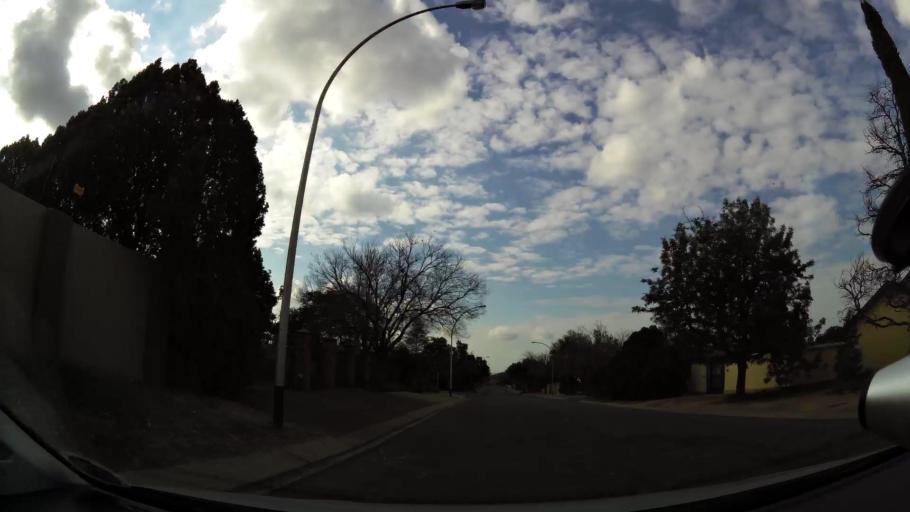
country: ZA
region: Orange Free State
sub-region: Mangaung Metropolitan Municipality
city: Bloemfontein
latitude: -29.0752
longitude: 26.2120
